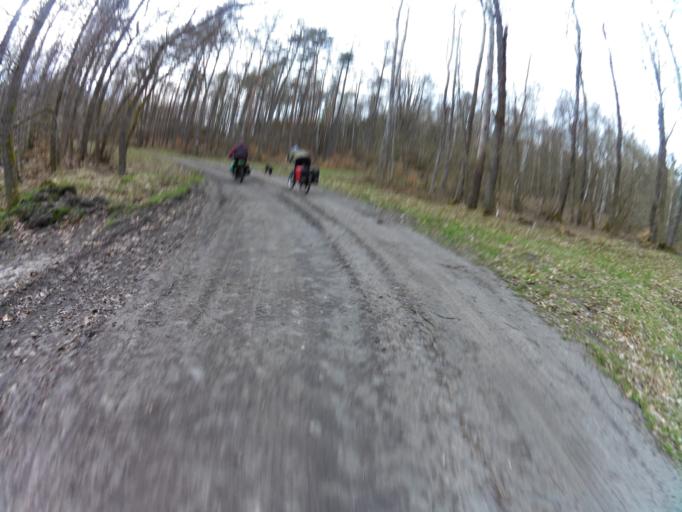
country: PL
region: West Pomeranian Voivodeship
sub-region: Powiat szczecinecki
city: Bialy Bor
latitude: 53.8964
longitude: 16.7171
